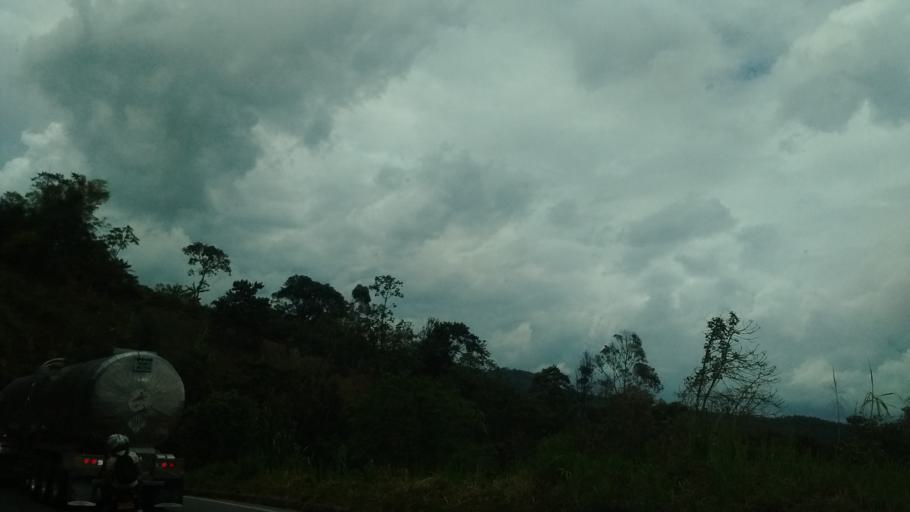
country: CO
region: Cauca
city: Rosas
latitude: 2.3101
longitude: -76.6861
